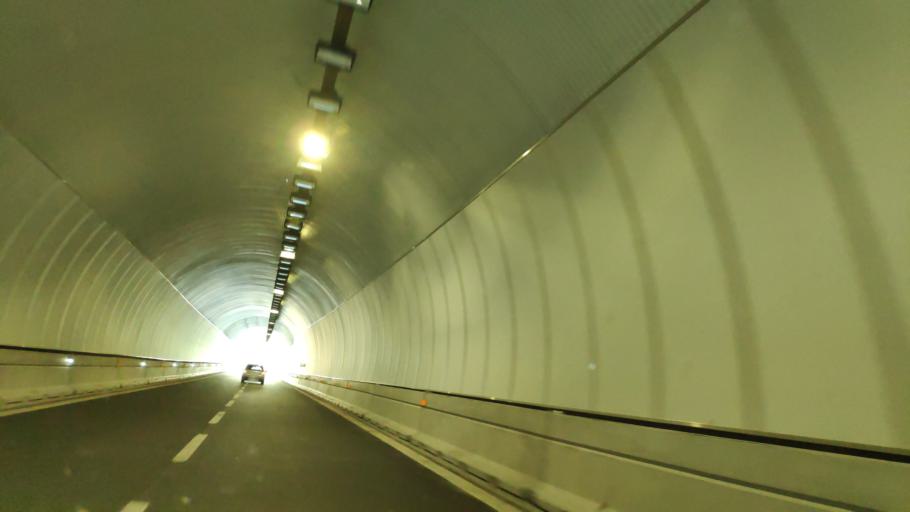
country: IT
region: Calabria
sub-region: Provincia di Cosenza
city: Belsito
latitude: 39.1641
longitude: 16.2904
